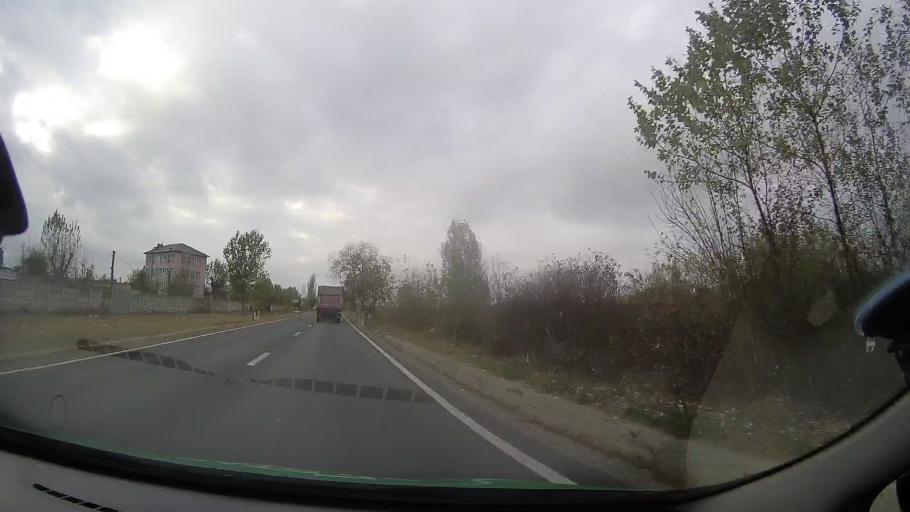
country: RO
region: Constanta
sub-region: Municipiul Medgidia
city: Medgidia
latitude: 44.2681
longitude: 28.2771
